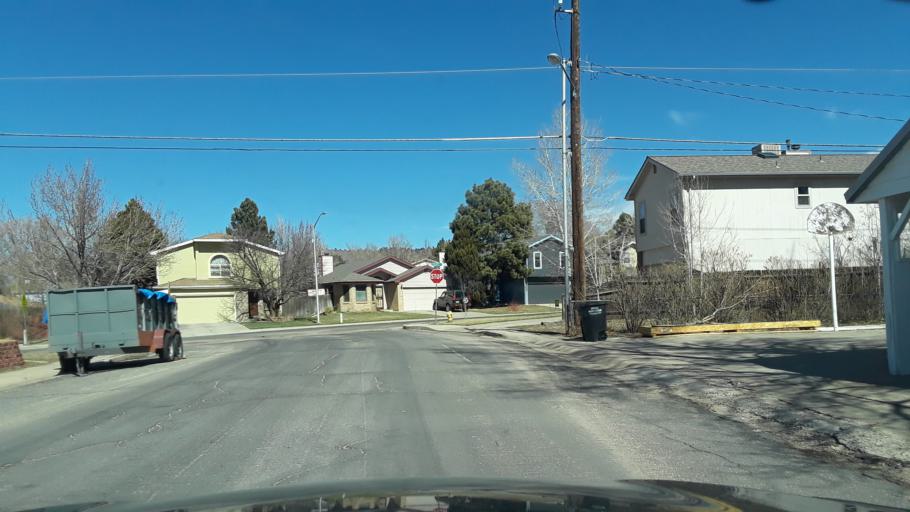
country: US
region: Colorado
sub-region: El Paso County
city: Colorado Springs
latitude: 38.8784
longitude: -104.8007
